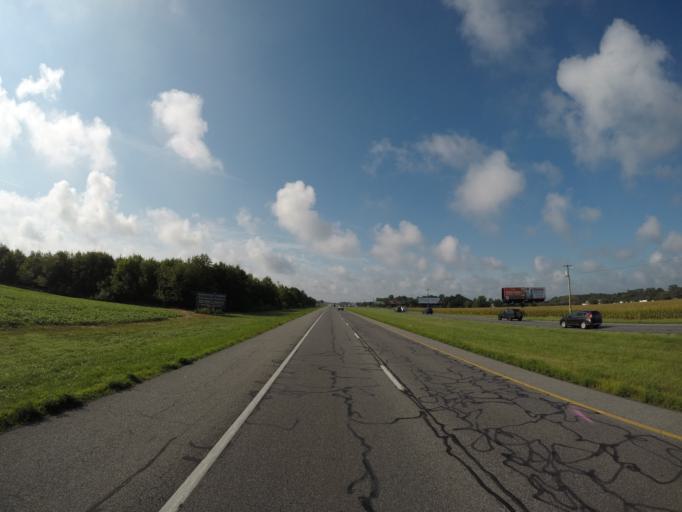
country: US
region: Delaware
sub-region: Sussex County
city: Bridgeville
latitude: 38.7334
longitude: -75.5913
